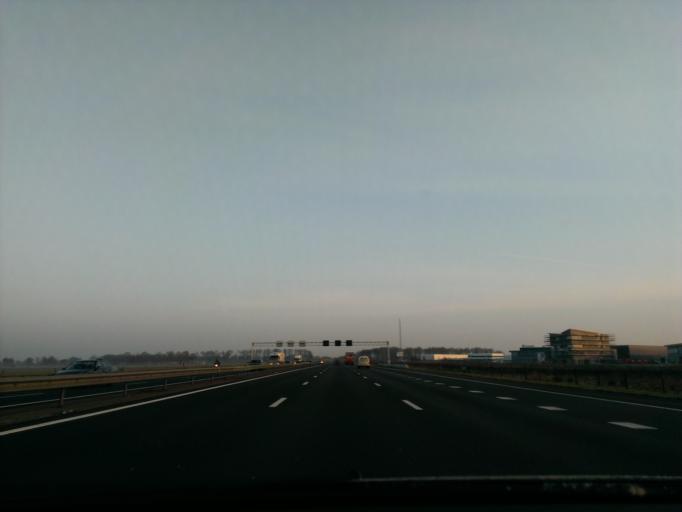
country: NL
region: Overijssel
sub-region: Gemeente Staphorst
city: Staphorst
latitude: 52.6267
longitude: 6.2065
